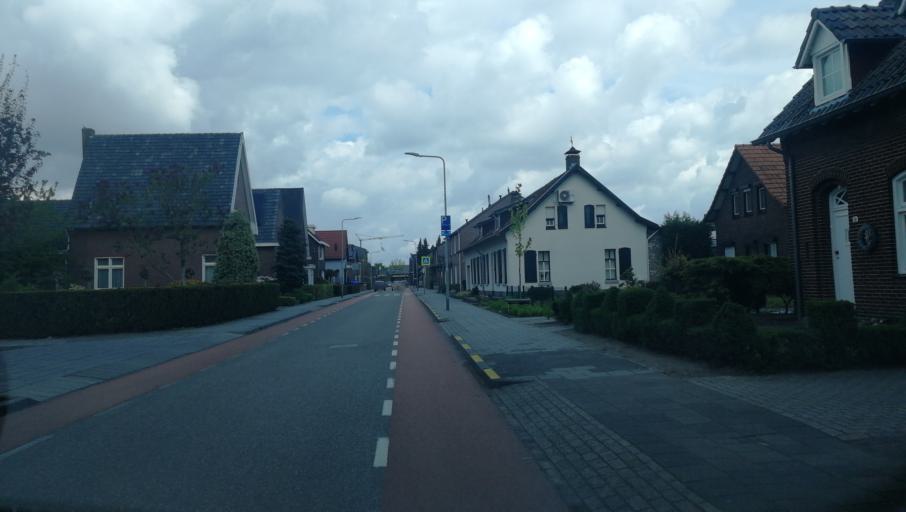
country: NL
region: Limburg
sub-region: Gemeente Peel en Maas
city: Maasbree
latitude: 51.3559
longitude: 6.0455
